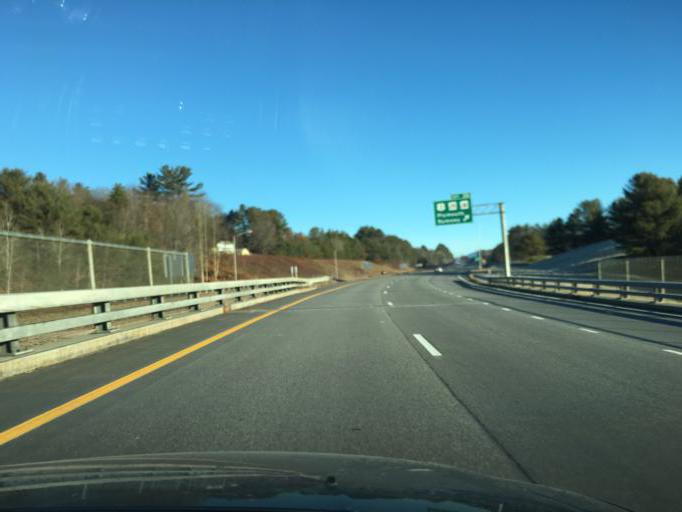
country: US
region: New Hampshire
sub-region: Grafton County
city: Plymouth
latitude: 43.7721
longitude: -71.6825
